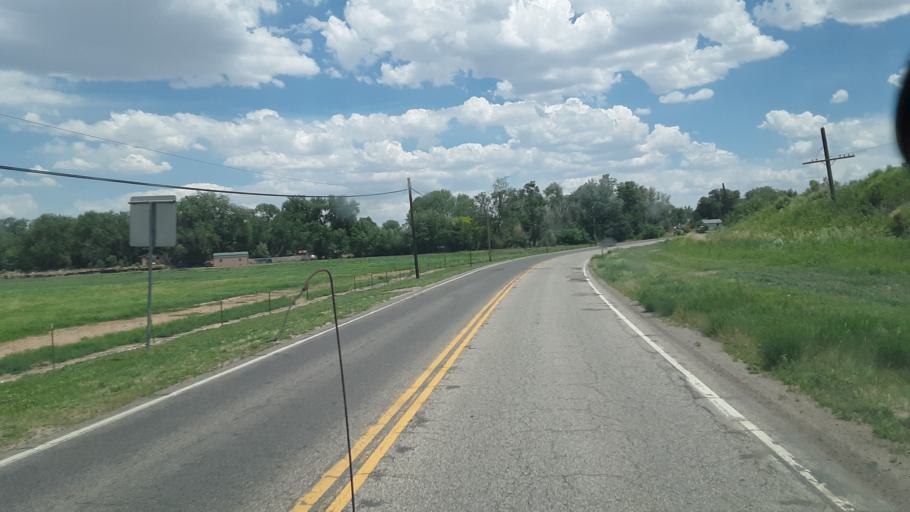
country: US
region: Colorado
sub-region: Fremont County
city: Florence
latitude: 38.4048
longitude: -105.1431
